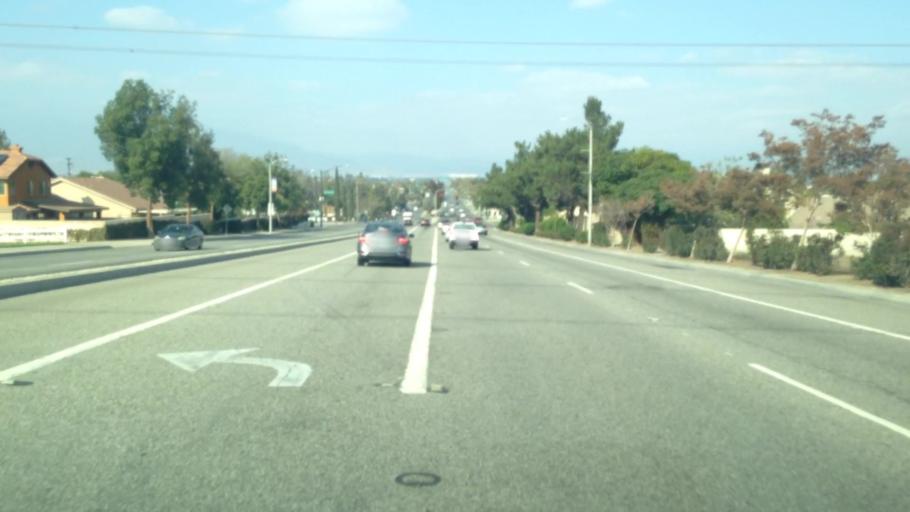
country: US
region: California
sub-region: Riverside County
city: Sunnyslope
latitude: 34.0464
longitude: -117.4354
